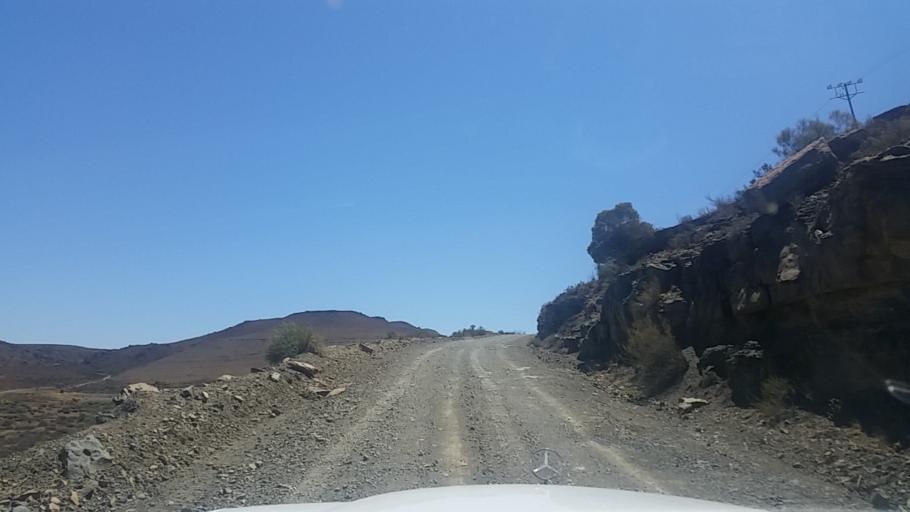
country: ZA
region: Eastern Cape
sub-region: Cacadu District Municipality
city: Graaff-Reinet
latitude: -31.8590
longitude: 24.5534
